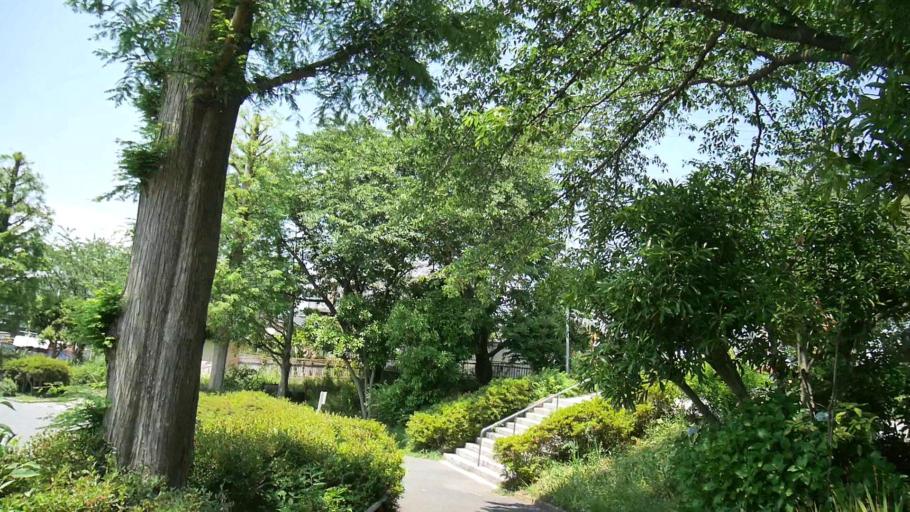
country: JP
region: Kanagawa
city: Fujisawa
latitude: 35.4030
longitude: 139.5167
